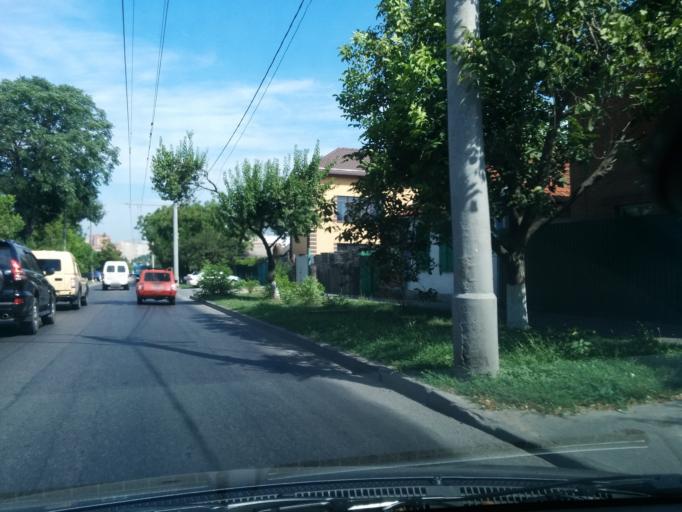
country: RU
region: Rostov
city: Severnyy
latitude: 47.2693
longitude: 39.7217
